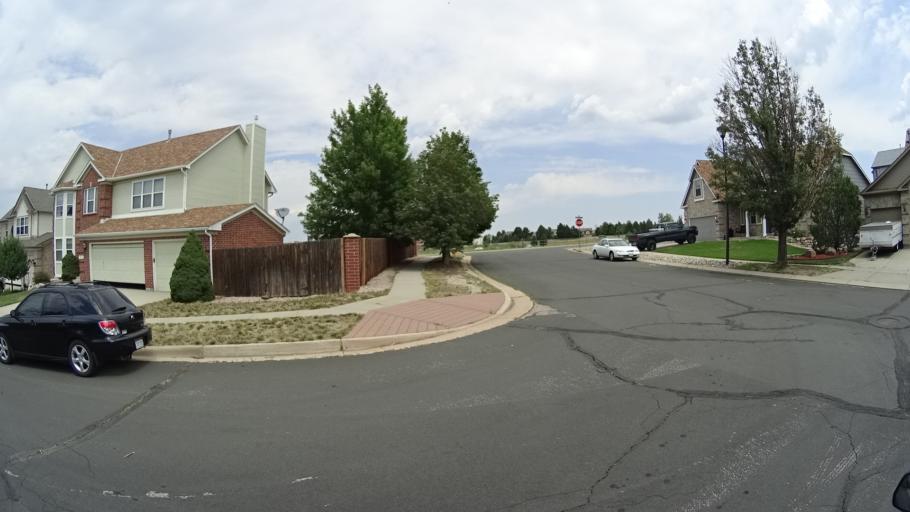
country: US
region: Colorado
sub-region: El Paso County
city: Black Forest
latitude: 38.9629
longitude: -104.7753
